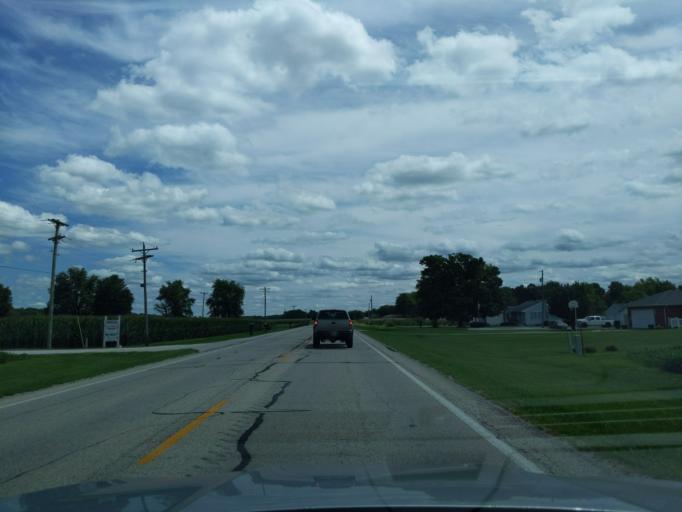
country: US
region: Indiana
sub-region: Ripley County
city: Batesville
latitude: 39.3084
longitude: -85.2720
